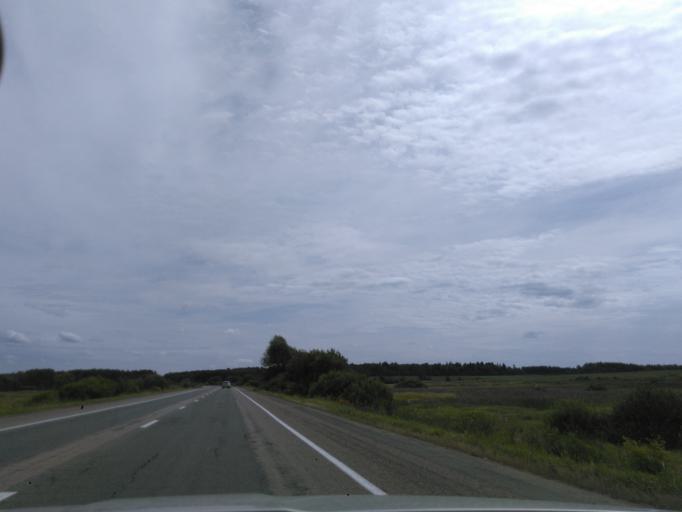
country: RU
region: Moskovskaya
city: Solnechnogorsk
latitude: 56.1510
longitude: 36.9272
